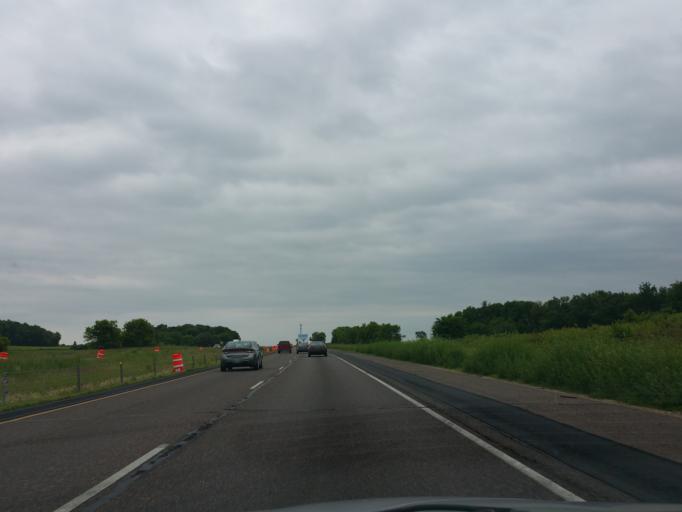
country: US
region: Wisconsin
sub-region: Dunn County
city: Colfax
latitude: 44.8656
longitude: -91.6868
